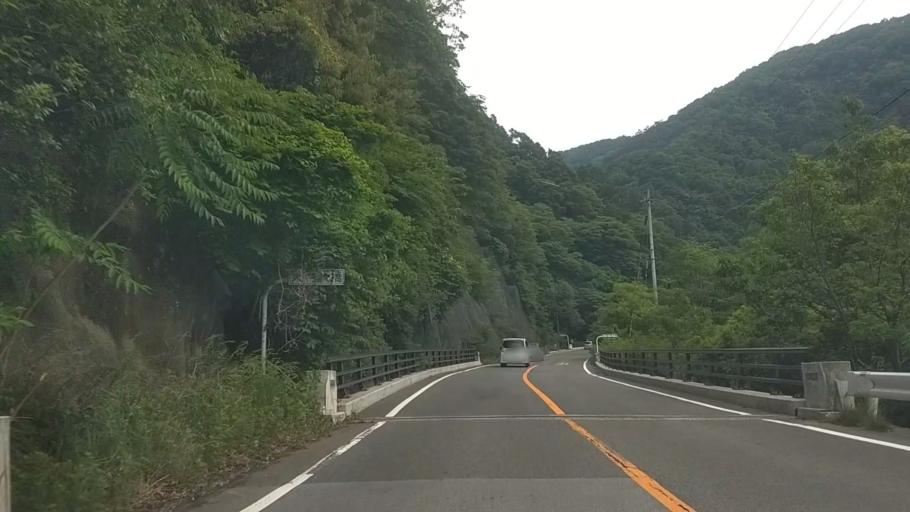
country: JP
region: Yamanashi
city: Isawa
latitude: 35.5600
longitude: 138.5897
